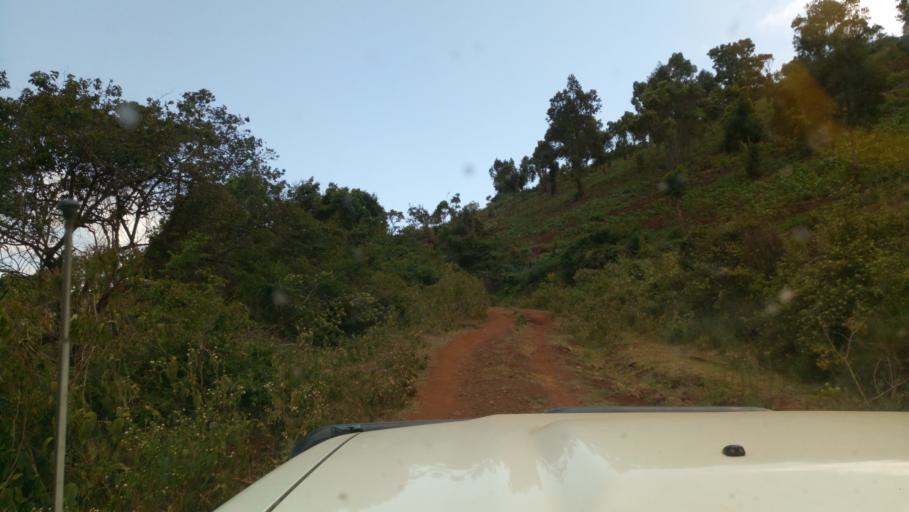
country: KE
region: Nyeri
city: Nyeri
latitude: -0.3129
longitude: 36.8431
